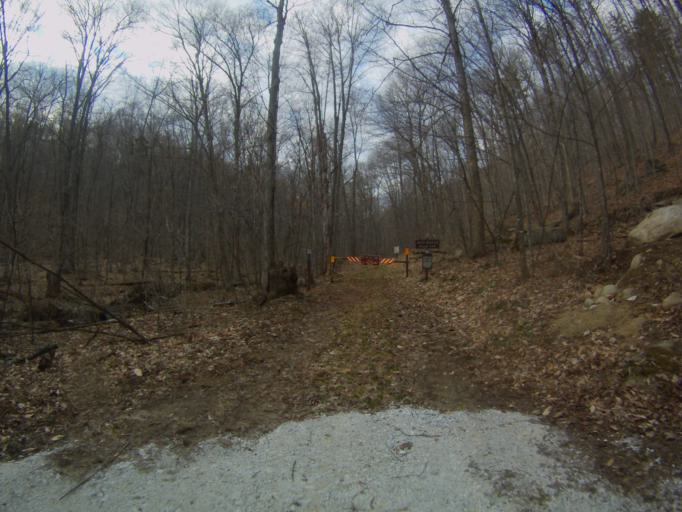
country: US
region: Vermont
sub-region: Rutland County
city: Brandon
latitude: 43.8454
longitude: -73.0423
